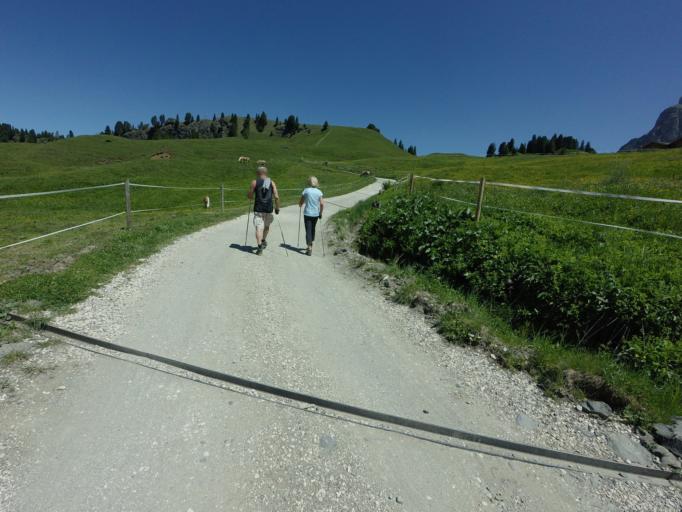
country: IT
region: Trentino-Alto Adige
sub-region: Provincia di Trento
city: Mazzin
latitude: 46.5111
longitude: 11.6858
